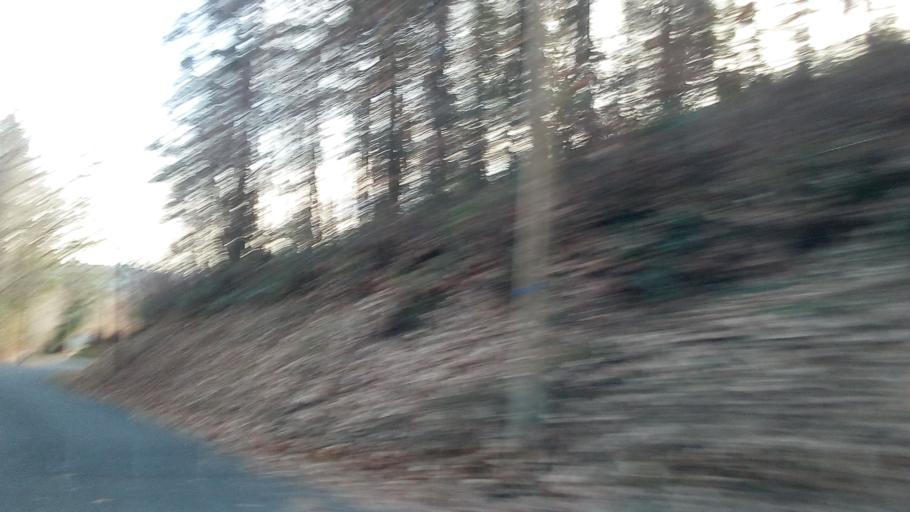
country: FR
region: Limousin
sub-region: Departement de la Correze
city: Naves
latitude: 45.3014
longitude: 1.7833
